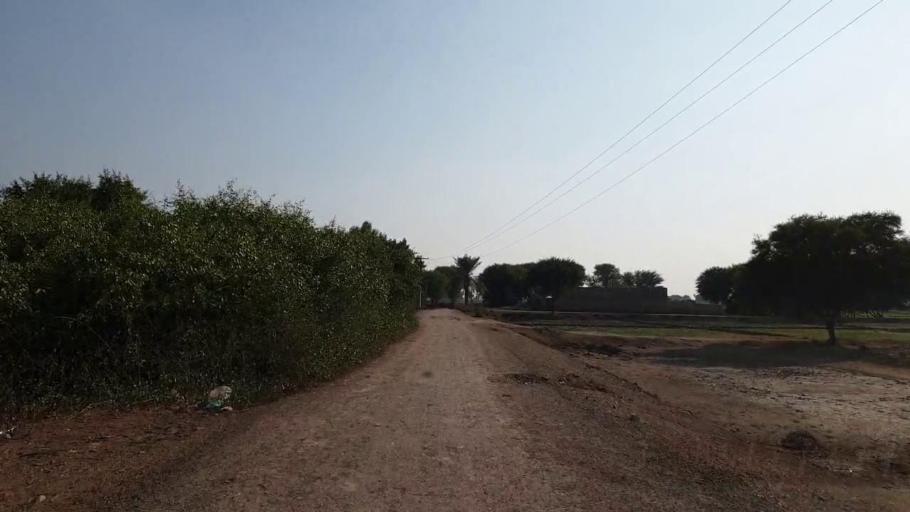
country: PK
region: Sindh
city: Sehwan
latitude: 26.4383
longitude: 67.8113
